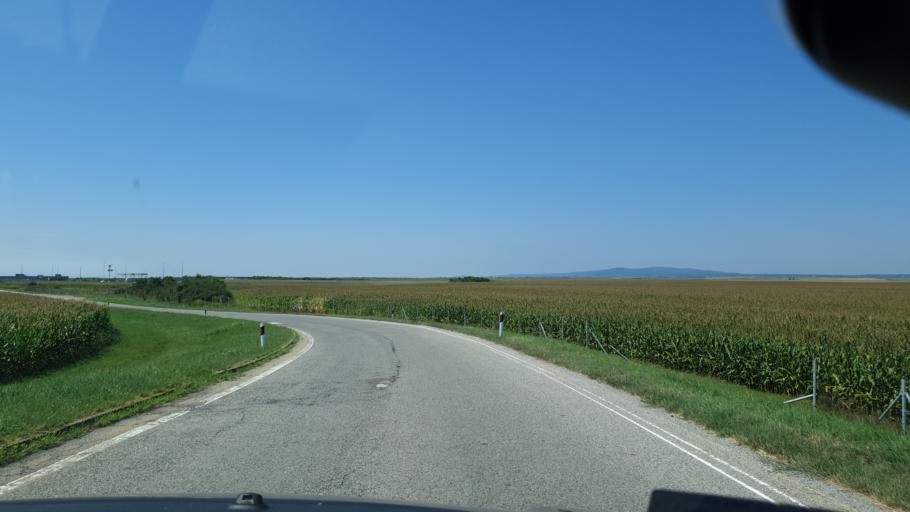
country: RS
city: Krcedin
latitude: 45.1013
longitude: 20.1098
